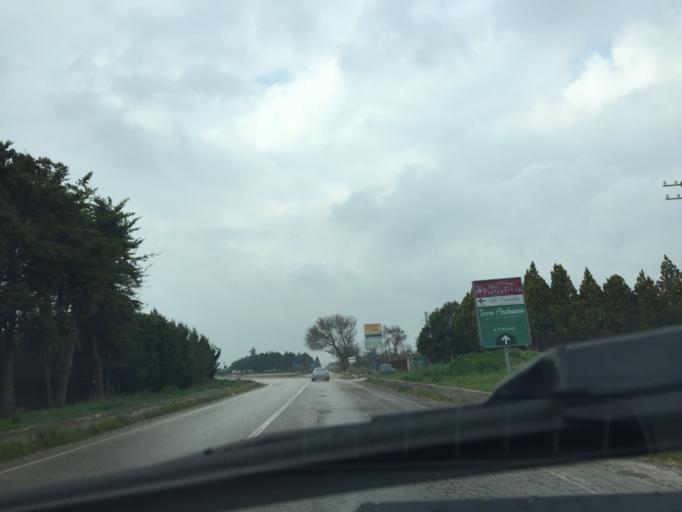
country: IT
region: Apulia
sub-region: Provincia di Foggia
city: Foggia
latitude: 41.4411
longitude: 15.4953
